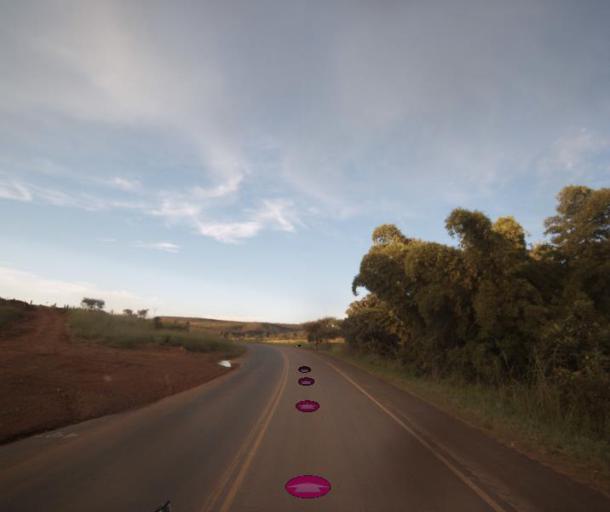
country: BR
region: Goias
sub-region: Anapolis
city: Anapolis
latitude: -16.1596
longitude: -48.8890
